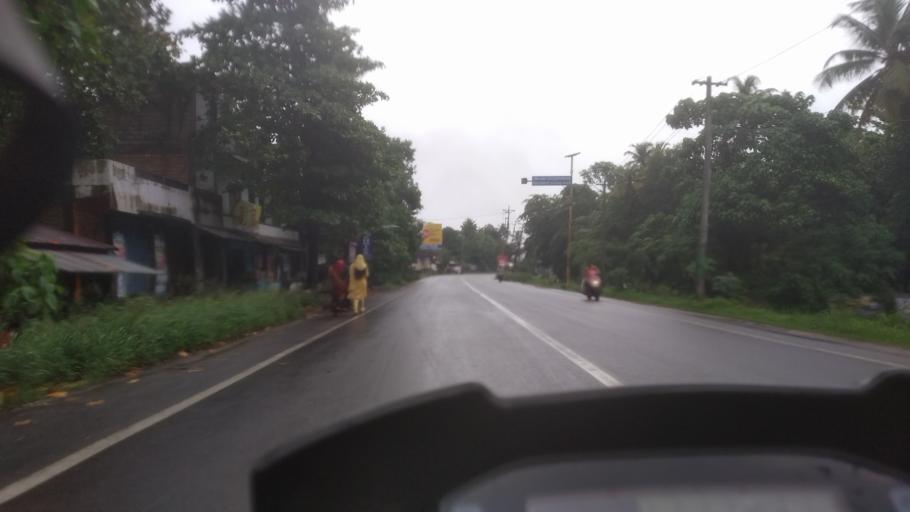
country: IN
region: Kerala
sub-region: Alappuzha
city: Kayankulam
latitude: 9.1432
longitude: 76.5121
